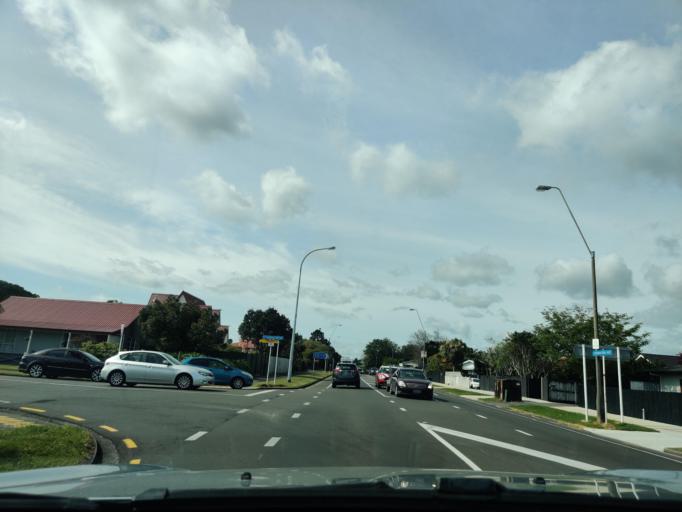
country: NZ
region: Taranaki
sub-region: New Plymouth District
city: New Plymouth
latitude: -39.0716
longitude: 174.0909
